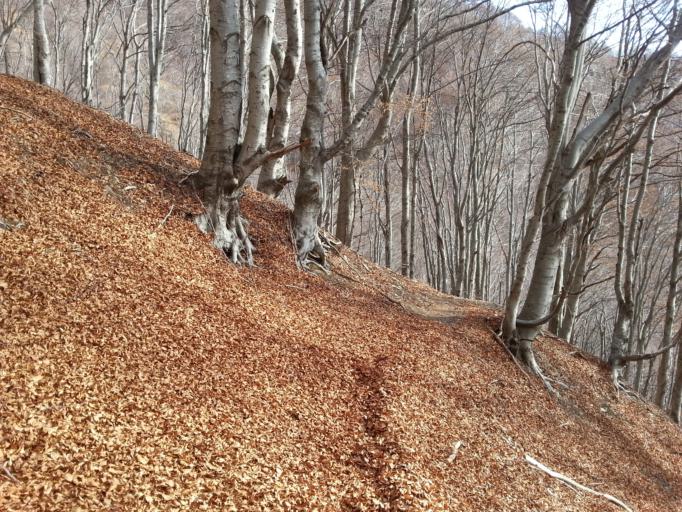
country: CH
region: Ticino
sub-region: Lugano District
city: Gravesano
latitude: 46.0724
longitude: 8.8740
